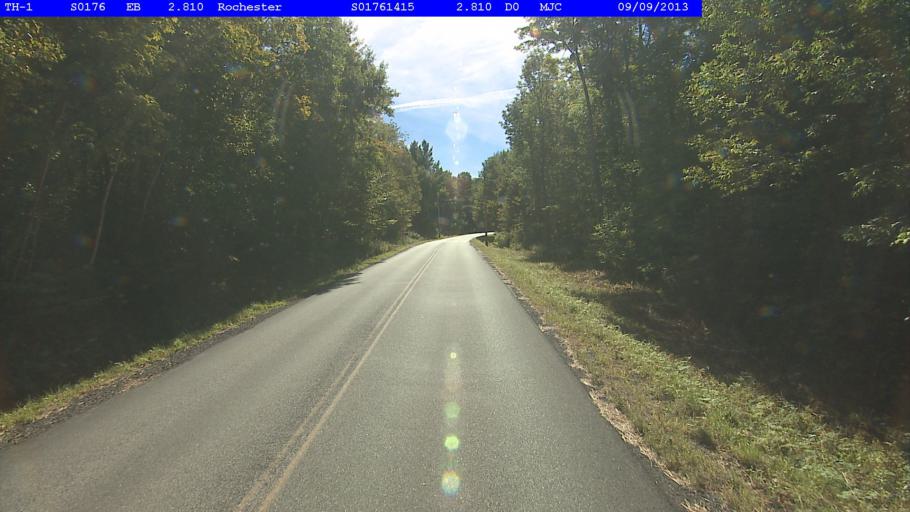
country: US
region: Vermont
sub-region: Orange County
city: Randolph
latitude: 43.8637
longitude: -72.7635
